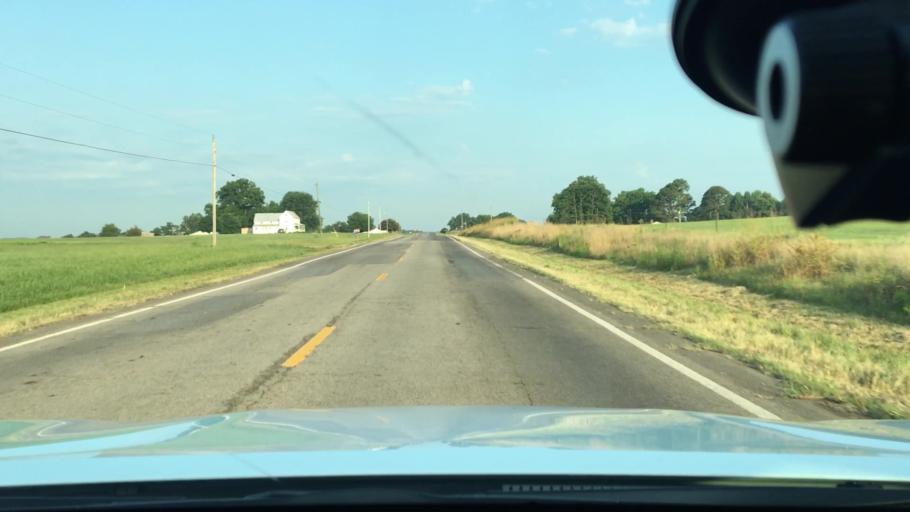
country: US
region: Arkansas
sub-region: Johnson County
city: Clarksville
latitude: 35.3788
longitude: -93.5405
